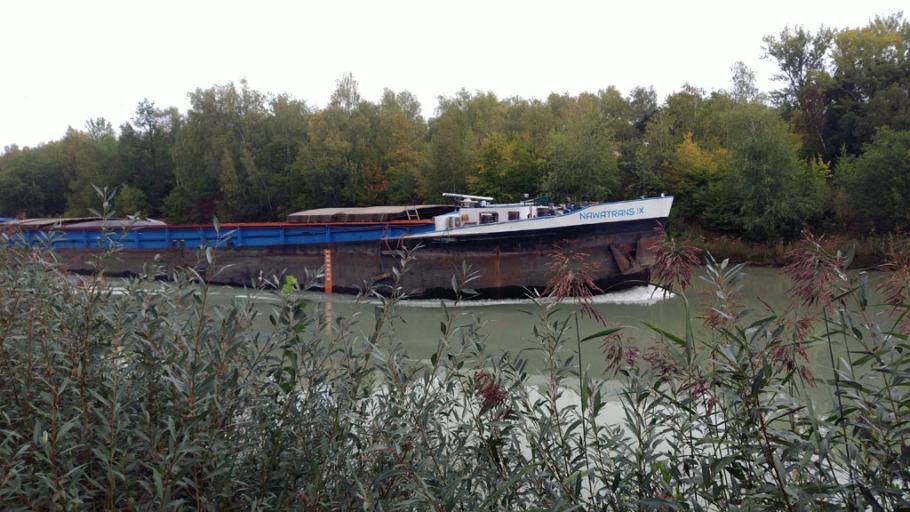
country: DE
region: Lower Saxony
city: Laatzen
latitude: 52.3408
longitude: 9.8818
